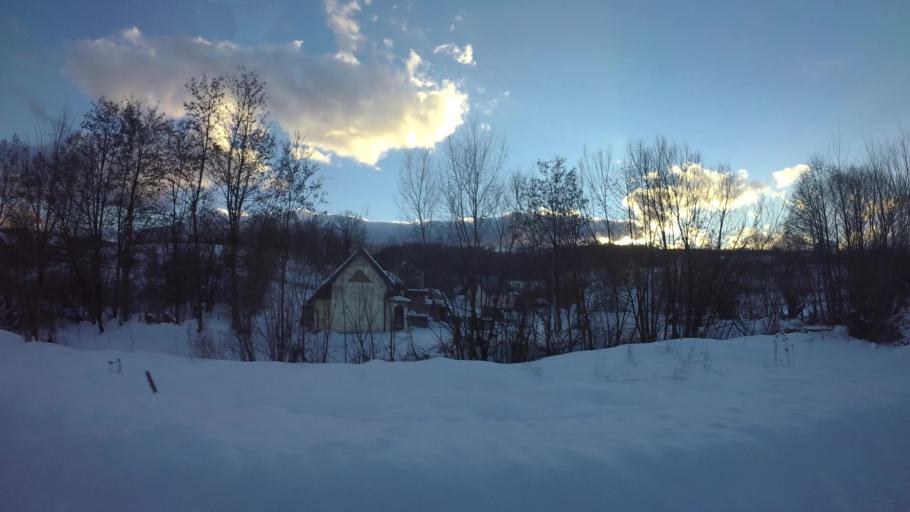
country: BA
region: Federation of Bosnia and Herzegovina
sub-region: Kanton Sarajevo
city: Sarajevo
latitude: 43.8076
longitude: 18.3665
